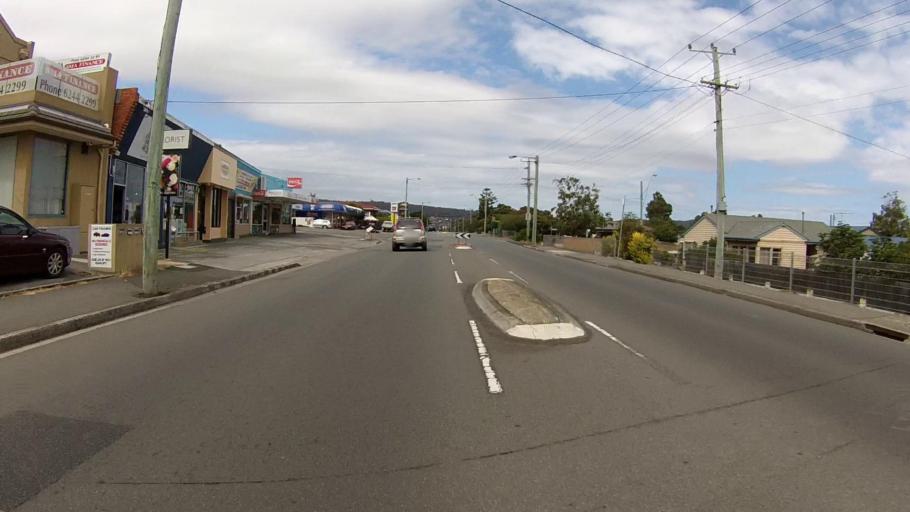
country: AU
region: Tasmania
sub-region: Clarence
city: Bellerive
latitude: -42.8752
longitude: 147.3780
